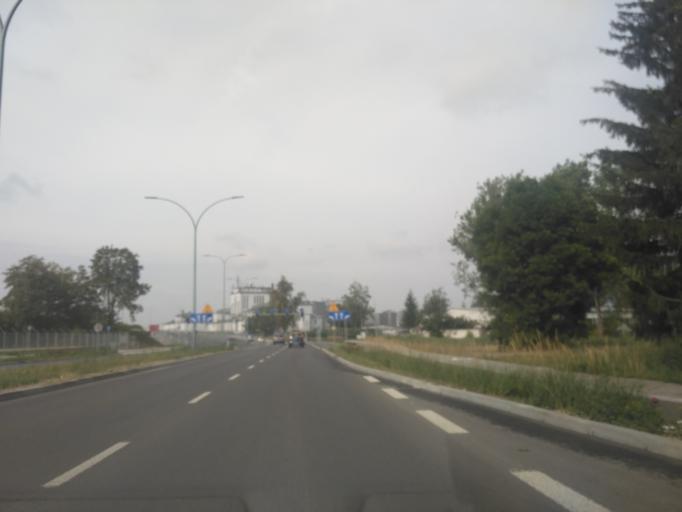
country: PL
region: Lublin Voivodeship
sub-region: Powiat lubelski
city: Lublin
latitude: 51.2230
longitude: 22.5597
